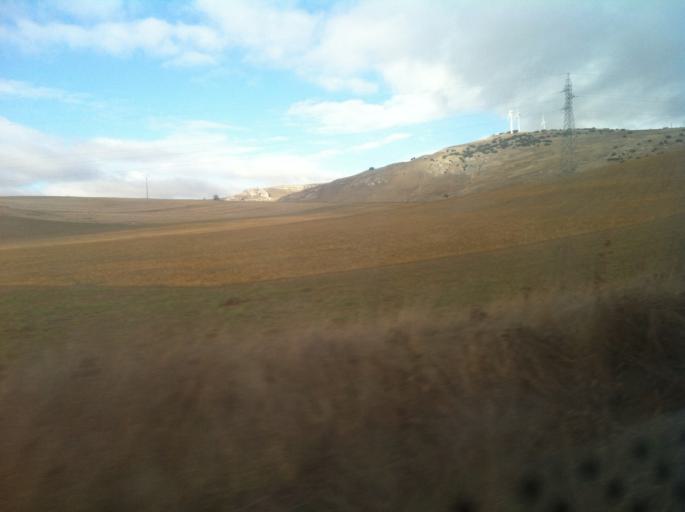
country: ES
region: Castille and Leon
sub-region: Provincia de Burgos
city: Santa Maria del Invierno
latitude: 42.4533
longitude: -3.4521
